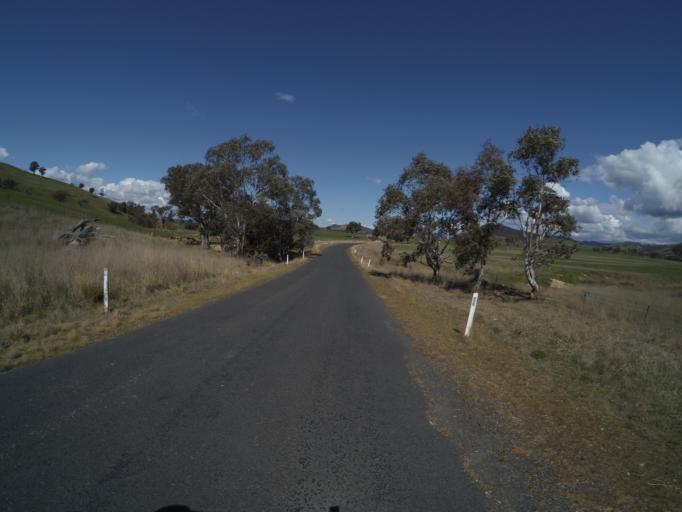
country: AU
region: New South Wales
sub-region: Yass Valley
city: Murrumbateman
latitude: -35.1184
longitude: 148.8652
